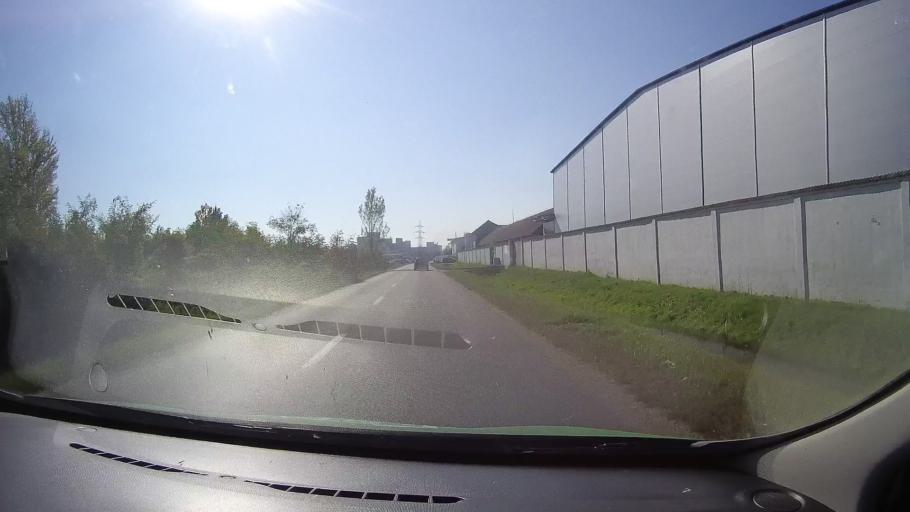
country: RO
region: Satu Mare
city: Carei
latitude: 47.7041
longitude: 22.4666
